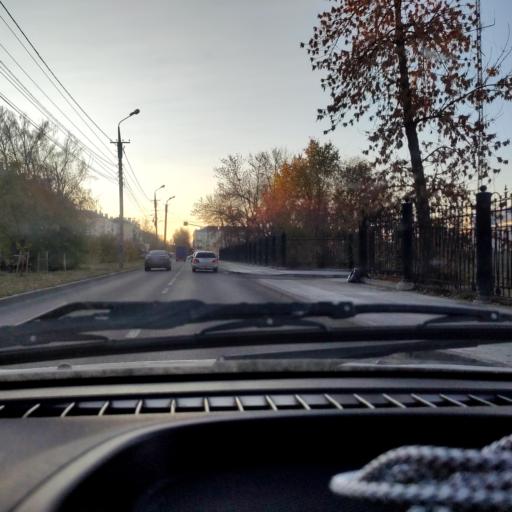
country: RU
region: Samara
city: Tol'yatti
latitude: 53.5152
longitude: 49.4086
